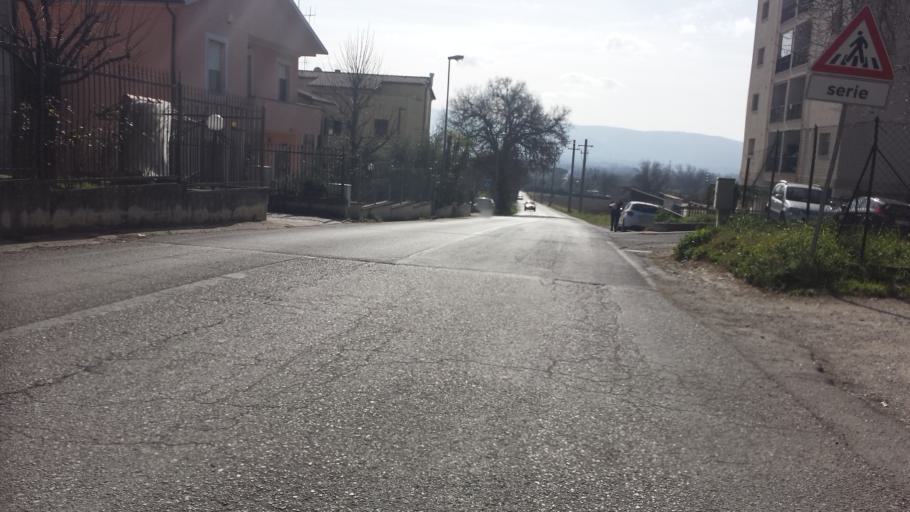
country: IT
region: Umbria
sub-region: Provincia di Terni
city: San Gemini
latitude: 42.5898
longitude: 12.5800
